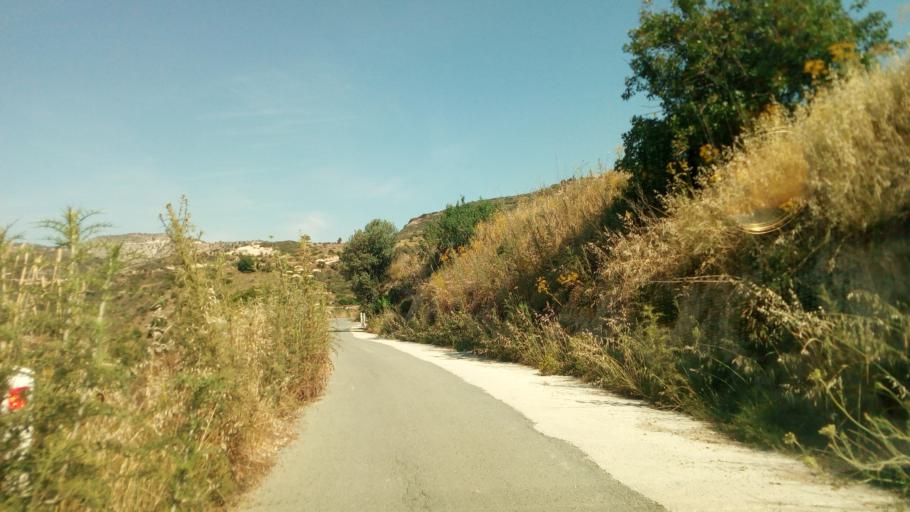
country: CY
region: Limassol
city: Pachna
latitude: 34.8154
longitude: 32.7334
